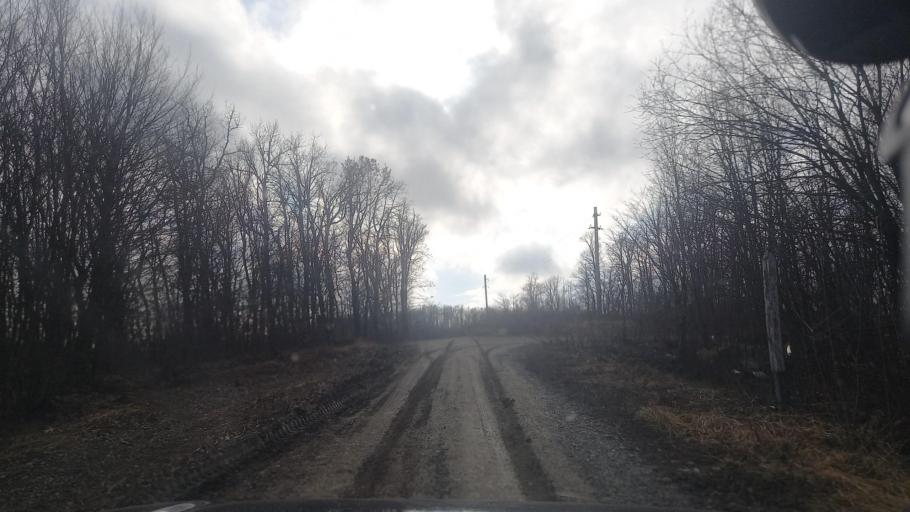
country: RU
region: Krasnodarskiy
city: Smolenskaya
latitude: 44.7450
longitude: 38.7779
